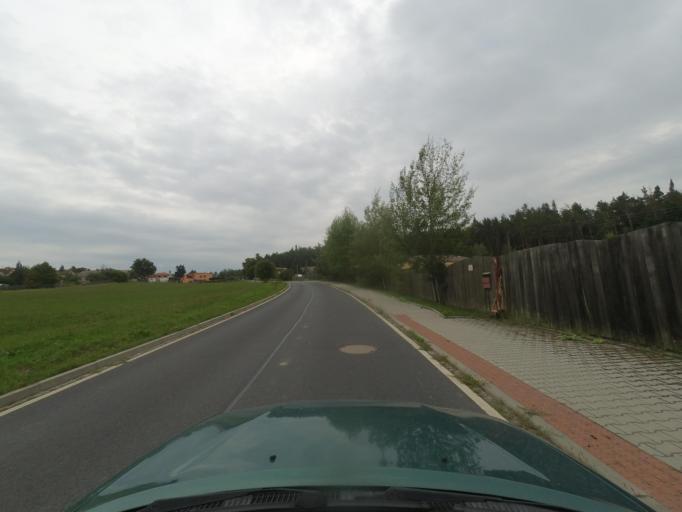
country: CZ
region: Plzensky
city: Stankov
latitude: 49.5426
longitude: 13.1060
